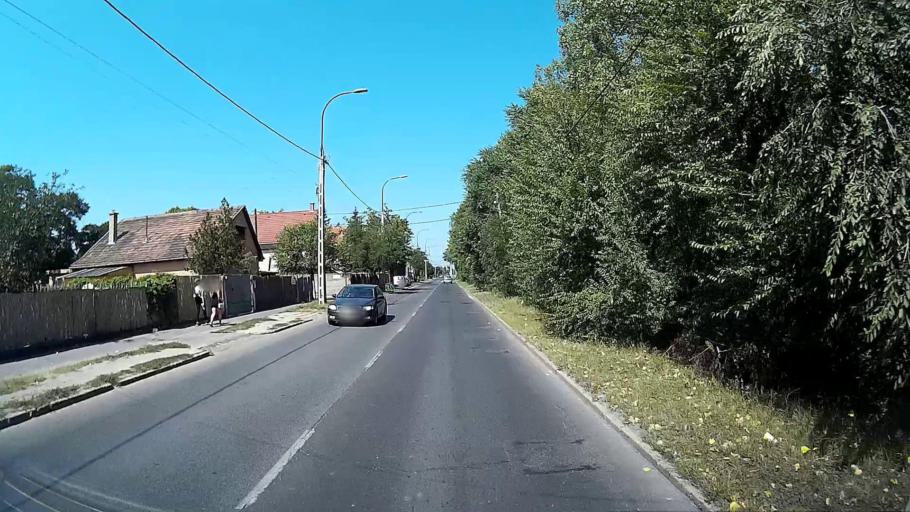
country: HU
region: Budapest
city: Budapest XXIII. keruelet
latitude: 47.4211
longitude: 19.1350
